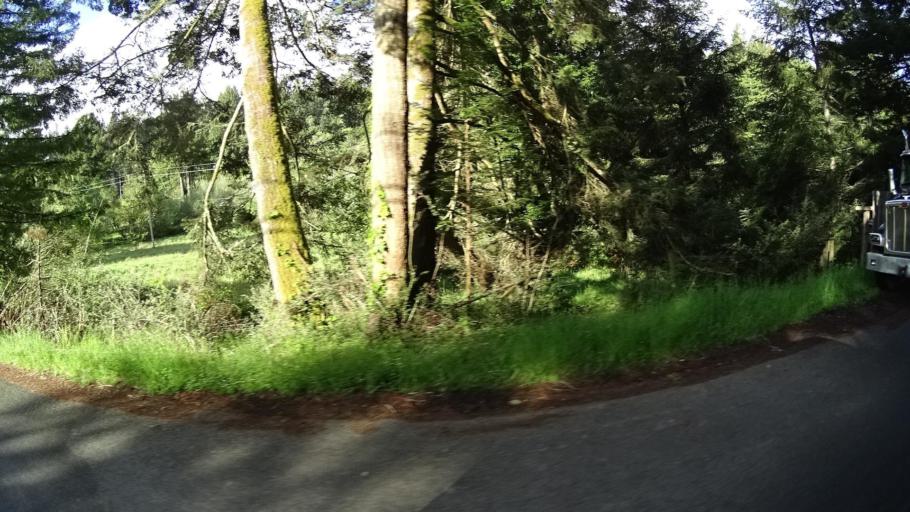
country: US
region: California
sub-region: Humboldt County
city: Arcata
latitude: 40.8967
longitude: -124.0451
